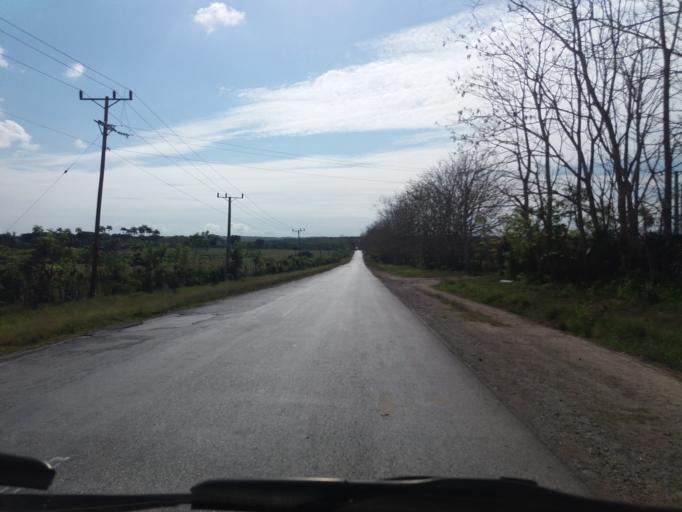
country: CU
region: Cienfuegos
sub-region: Municipio de Cienfuegos
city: Cienfuegos
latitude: 22.1656
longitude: -80.3793
